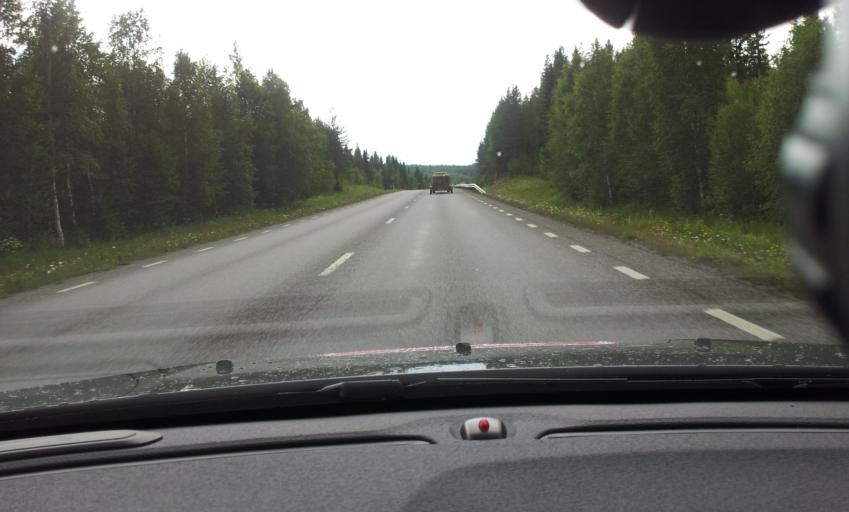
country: SE
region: Jaemtland
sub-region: Krokoms Kommun
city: Valla
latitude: 63.3118
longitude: 13.7625
